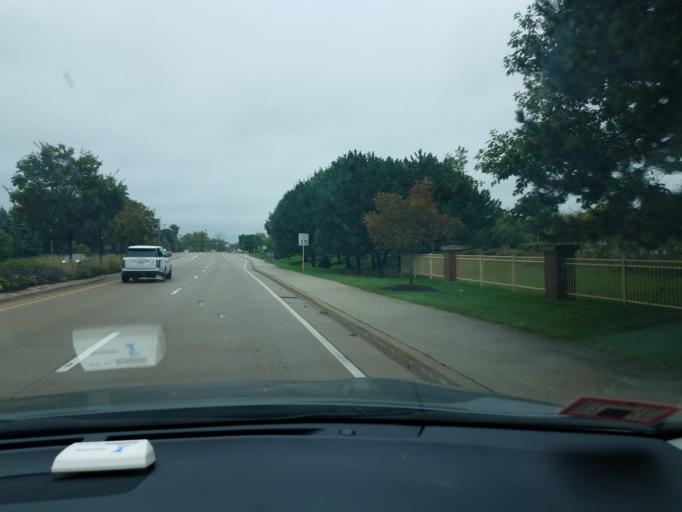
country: US
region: Illinois
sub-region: Lake County
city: Lincolnshire
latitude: 42.1968
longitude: -87.9419
